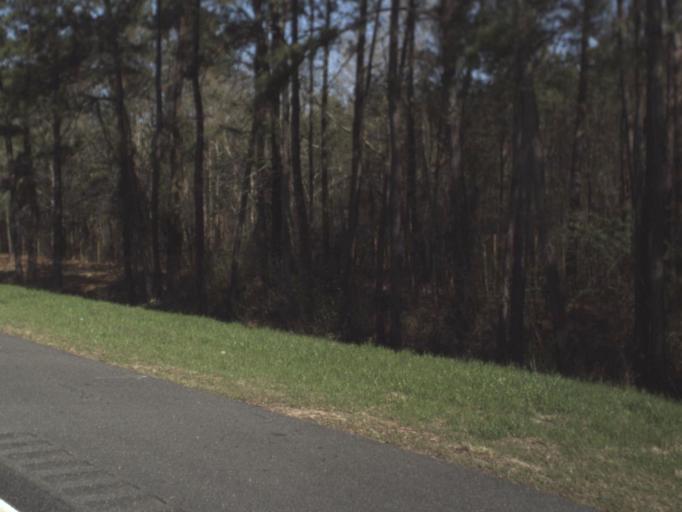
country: US
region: Florida
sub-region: Gadsden County
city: Midway
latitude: 30.5031
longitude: -84.4574
